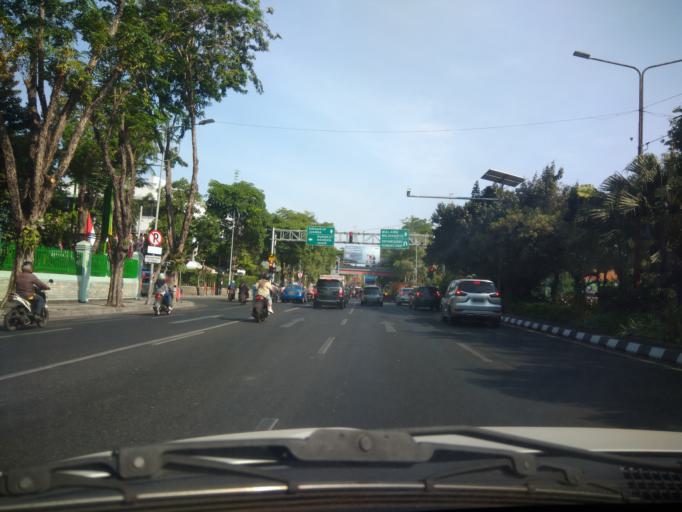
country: ID
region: East Java
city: Jagirsidosermo
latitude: -7.2949
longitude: 112.7392
